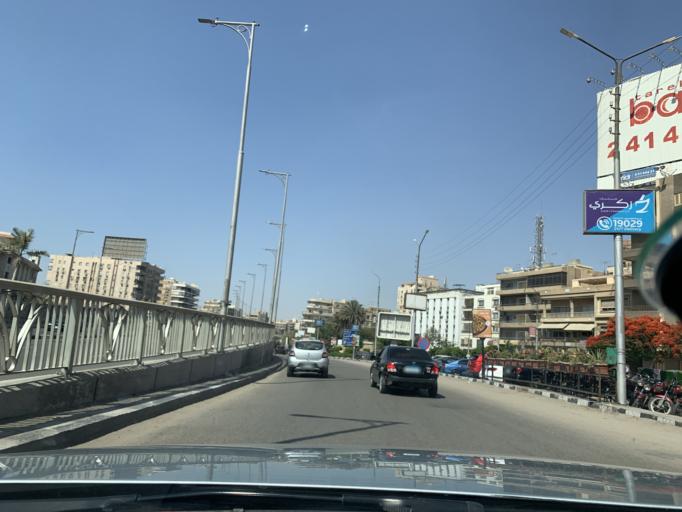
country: EG
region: Muhafazat al Qahirah
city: Cairo
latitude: 30.0853
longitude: 31.3332
